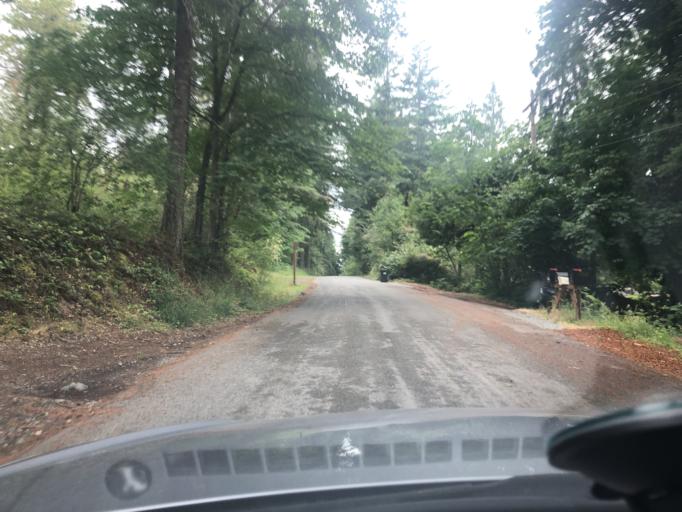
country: US
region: Washington
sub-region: King County
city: Black Diamond
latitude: 47.3224
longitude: -122.0326
